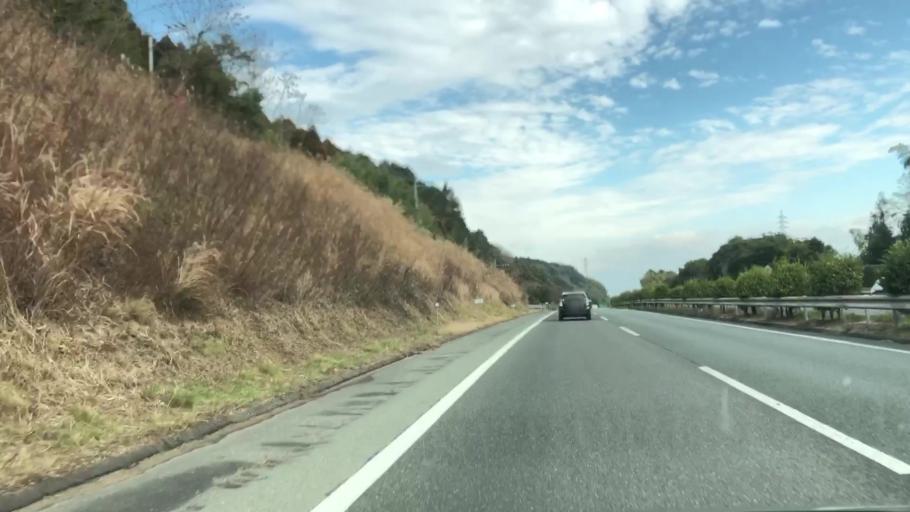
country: JP
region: Saga Prefecture
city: Tosu
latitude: 33.3919
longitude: 130.4922
